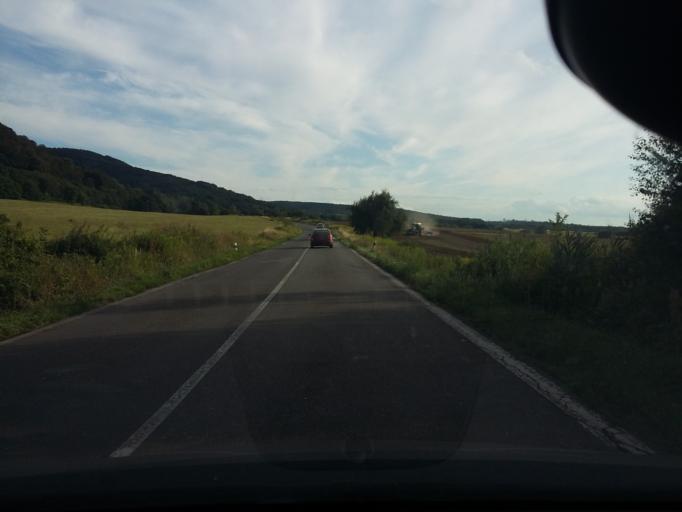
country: SK
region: Bratislavsky
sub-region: Okres Malacky
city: Malacky
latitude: 48.3789
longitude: 17.1498
